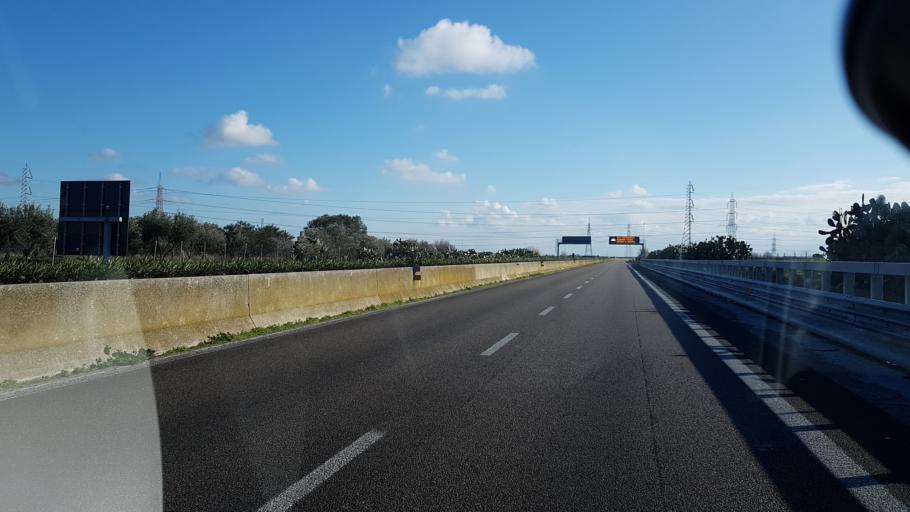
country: IT
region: Apulia
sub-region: Provincia di Brindisi
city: La Rosa
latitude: 40.6107
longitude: 17.9610
